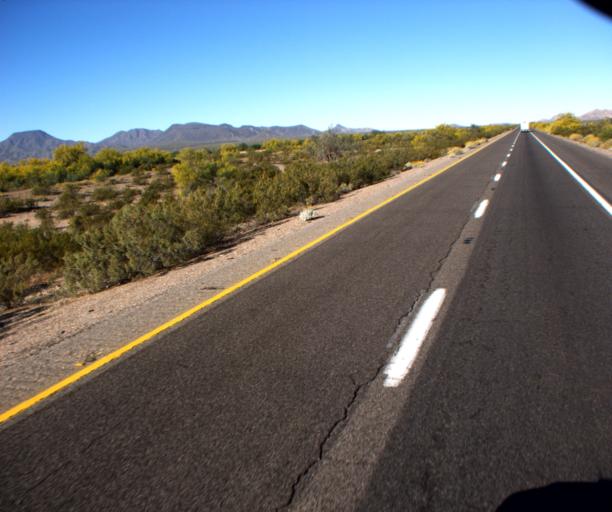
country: US
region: Arizona
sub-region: Pinal County
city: Maricopa
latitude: 32.8304
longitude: -112.0201
